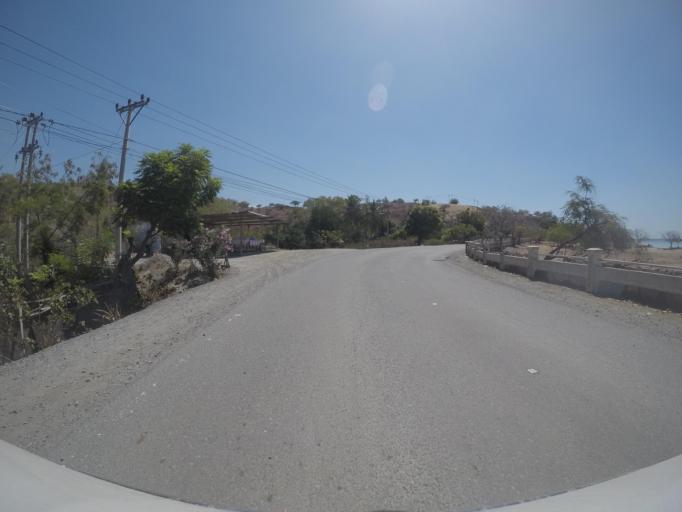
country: TL
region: Liquica
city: Liquica
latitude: -8.5694
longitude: 125.4396
